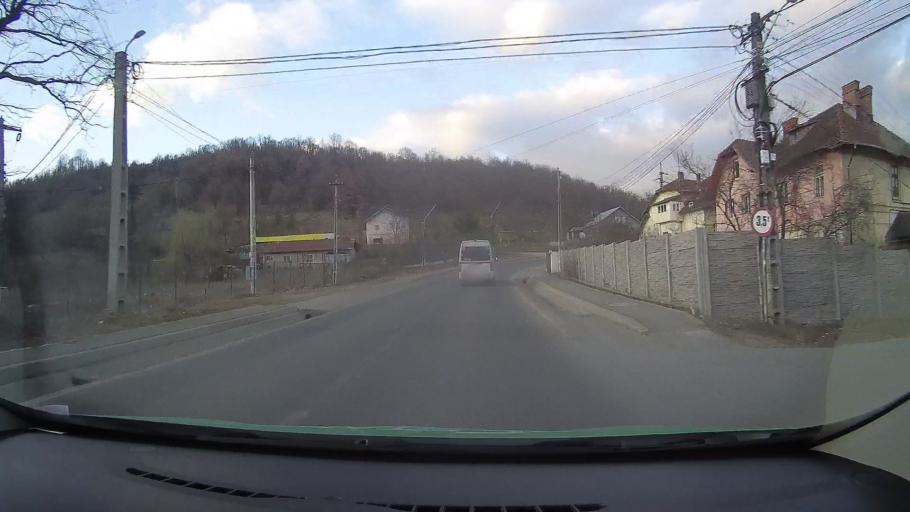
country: RO
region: Dambovita
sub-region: Municipiul Moreni
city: Moreni
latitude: 44.9776
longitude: 25.6201
